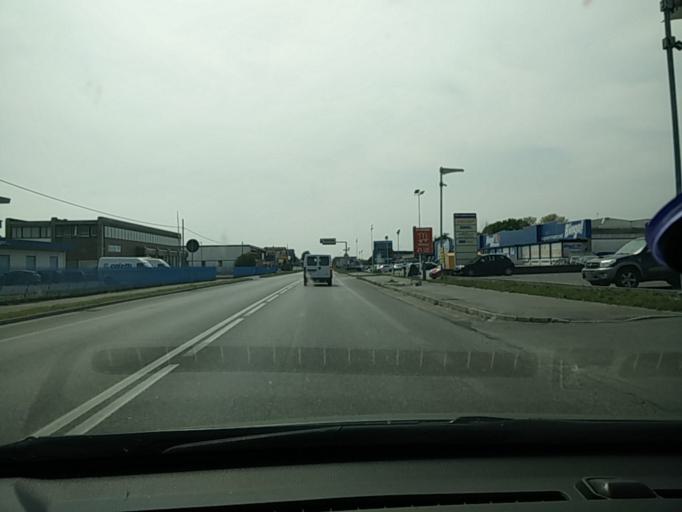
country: IT
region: Veneto
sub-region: Provincia di Treviso
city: San Vendemiano-Fossamerlo
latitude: 45.8897
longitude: 12.3243
